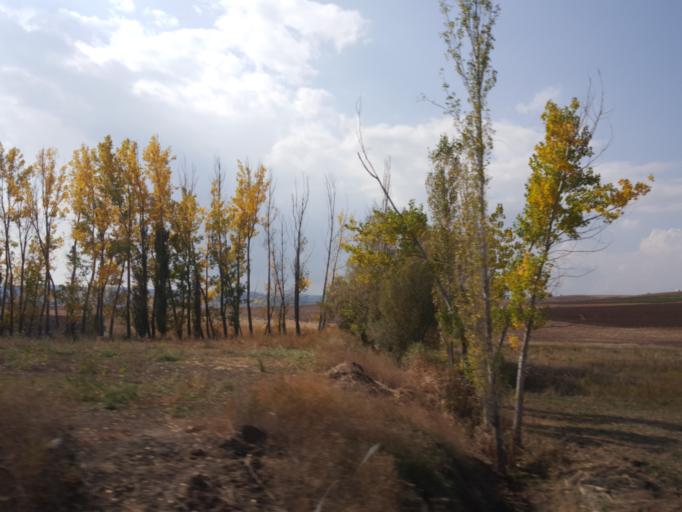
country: TR
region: Corum
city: Alaca
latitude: 40.1522
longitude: 34.8793
